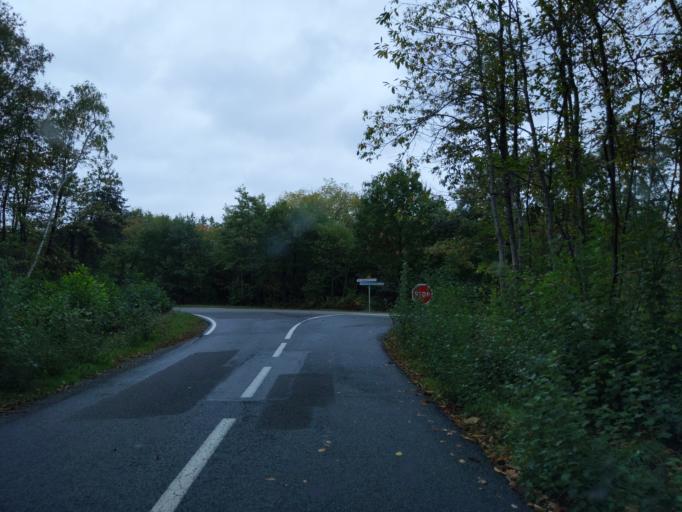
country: FR
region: Ile-de-France
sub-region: Departement des Yvelines
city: Saint-Arnoult-en-Yvelines
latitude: 48.5898
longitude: 1.9335
